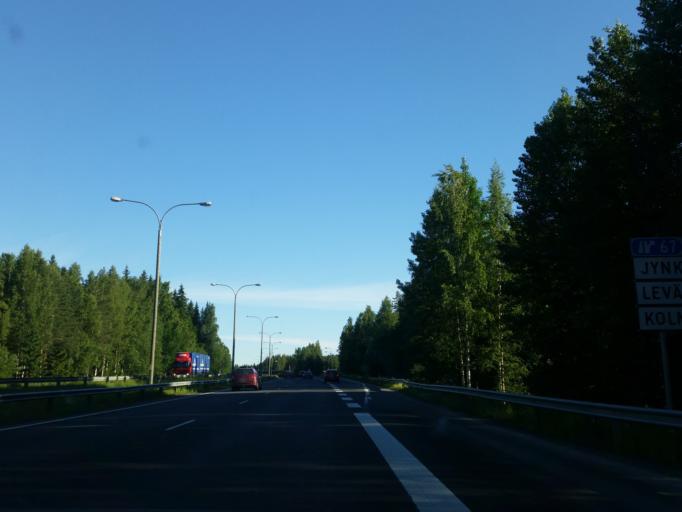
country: FI
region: Northern Savo
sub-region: Kuopio
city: Kuopio
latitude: 62.8671
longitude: 27.6184
